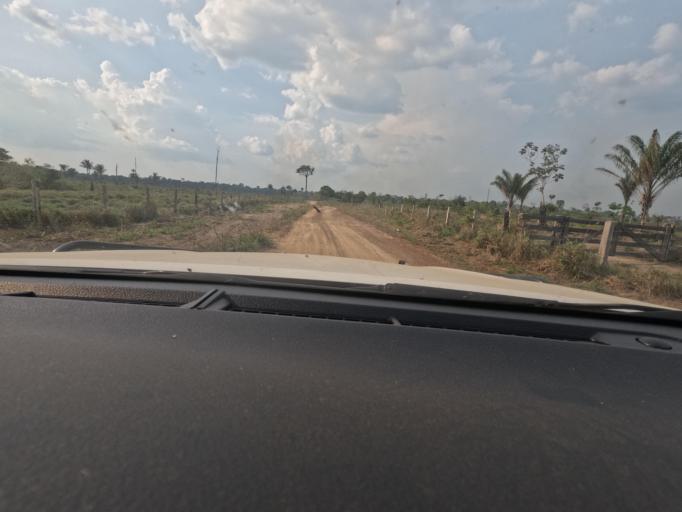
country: BR
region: Rondonia
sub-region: Porto Velho
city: Porto Velho
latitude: -8.6403
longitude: -63.1557
